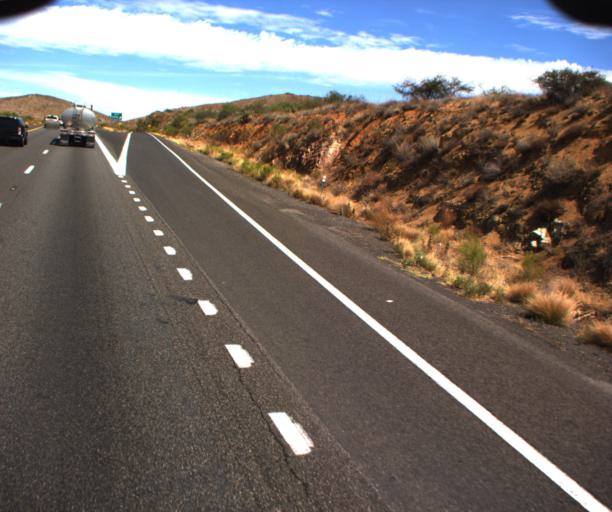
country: US
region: Arizona
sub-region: Yavapai County
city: Cordes Lakes
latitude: 34.2807
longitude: -112.1179
